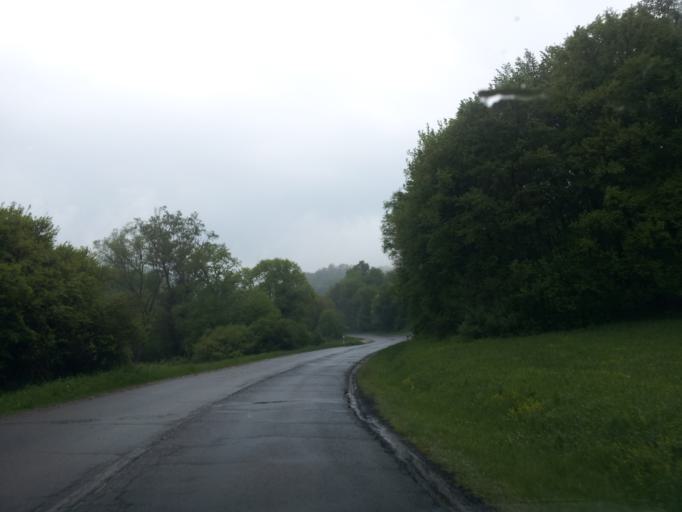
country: HU
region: Baranya
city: Komlo
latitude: 46.1990
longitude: 18.3037
